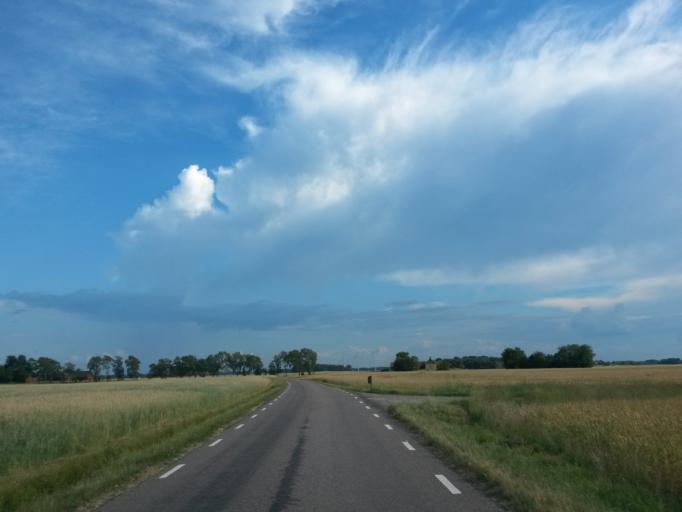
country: SE
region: Vaestra Goetaland
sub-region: Grastorps Kommun
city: Graestorp
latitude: 58.3648
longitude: 12.7827
